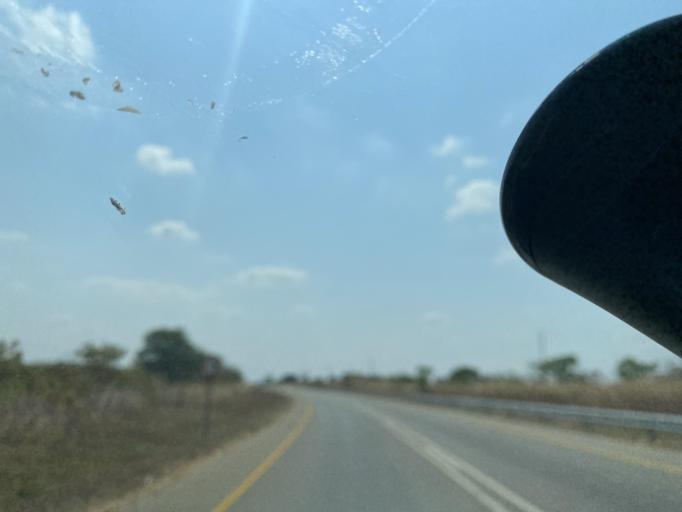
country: ZM
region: Lusaka
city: Chongwe
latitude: -15.5357
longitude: 28.6493
